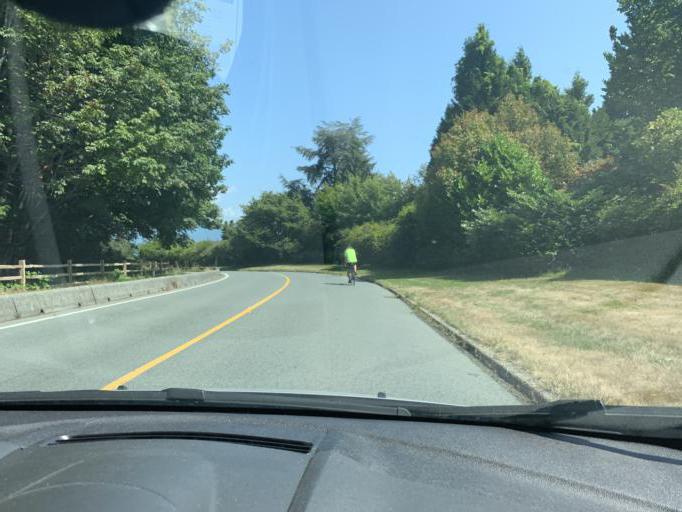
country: CA
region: British Columbia
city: West End
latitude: 49.2741
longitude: -123.2529
